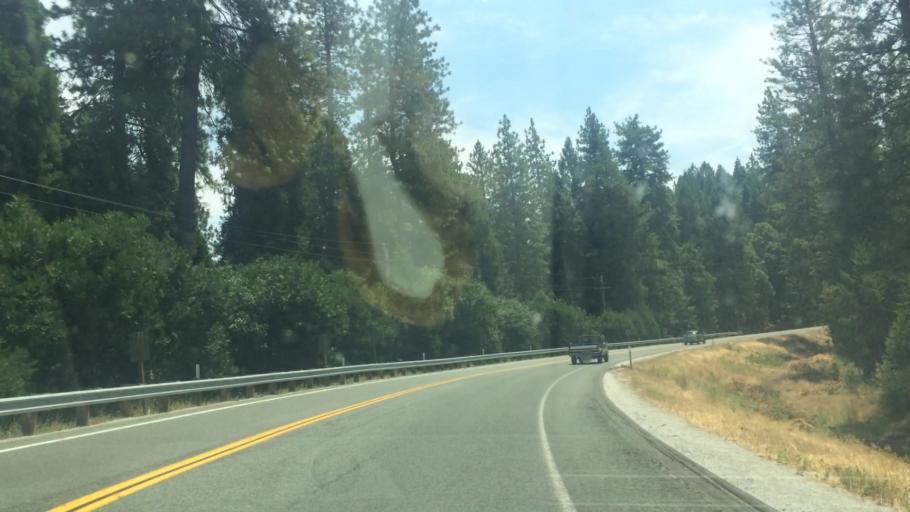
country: US
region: California
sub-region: Amador County
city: Pioneer
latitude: 38.4511
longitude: -120.5279
